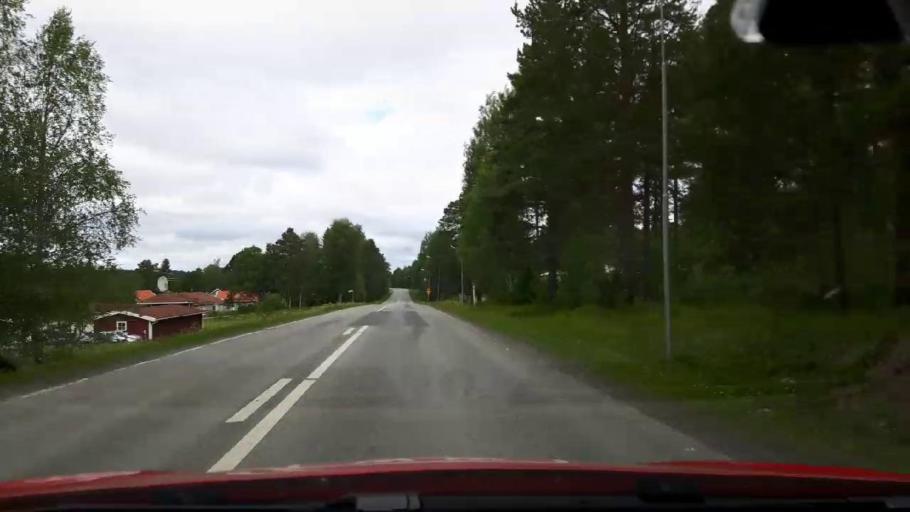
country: SE
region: Jaemtland
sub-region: Krokoms Kommun
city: Krokom
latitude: 63.2963
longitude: 14.4850
